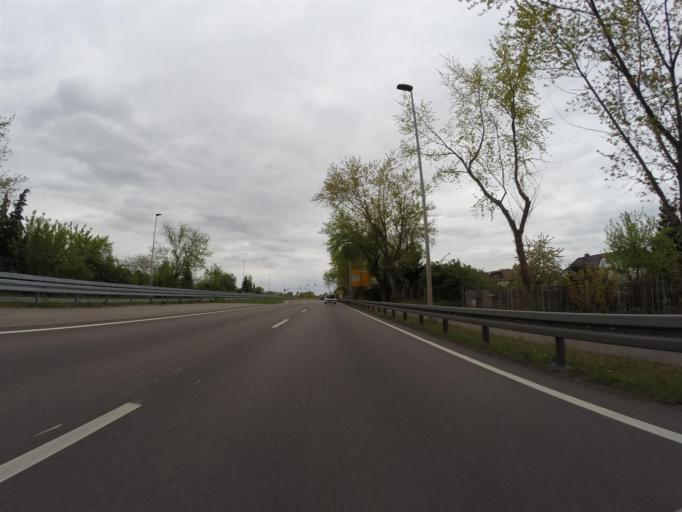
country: DE
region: Saxony-Anhalt
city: Schkopau
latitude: 51.3822
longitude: 11.9810
